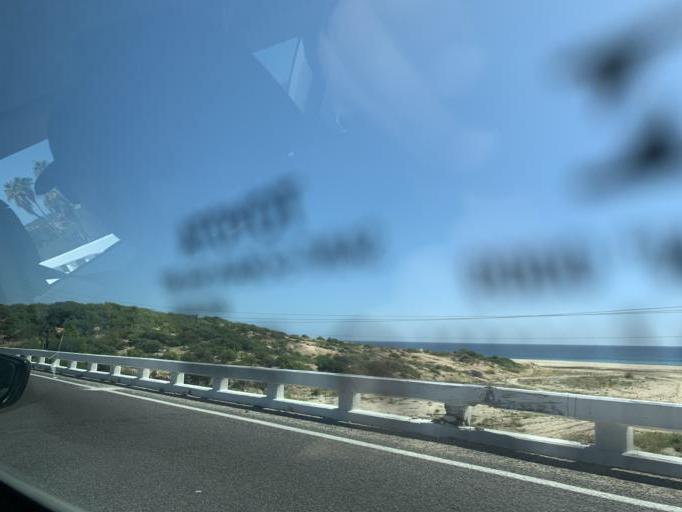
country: MX
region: Baja California Sur
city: Cabo San Lucas
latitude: 22.9624
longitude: -109.8011
